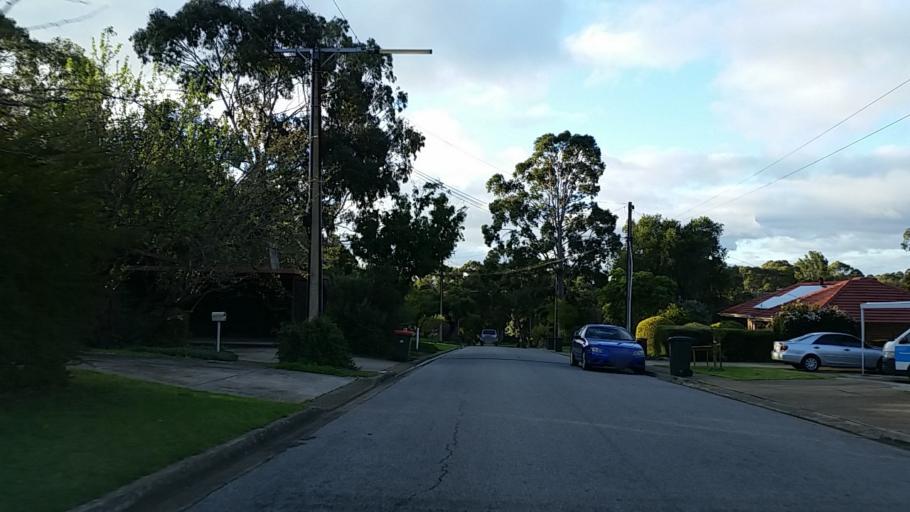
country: AU
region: South Australia
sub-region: Tea Tree Gully
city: Hope Valley
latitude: -34.8466
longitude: 138.7038
